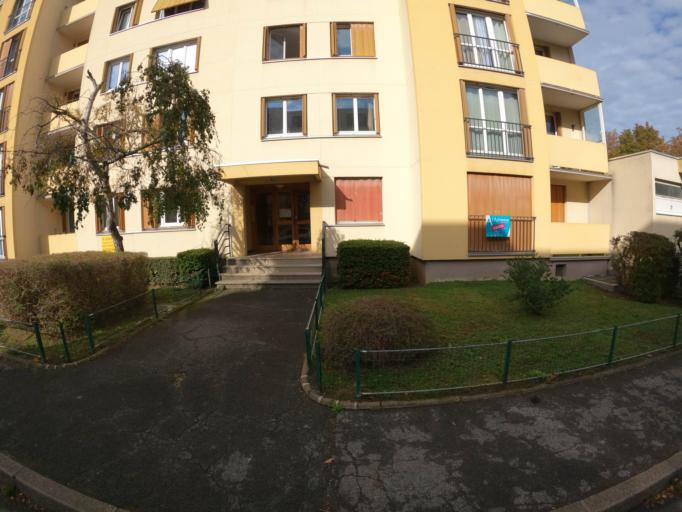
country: FR
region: Ile-de-France
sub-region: Departement de Seine-et-Marne
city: Brou-sur-Chantereine
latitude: 48.8860
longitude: 2.6285
